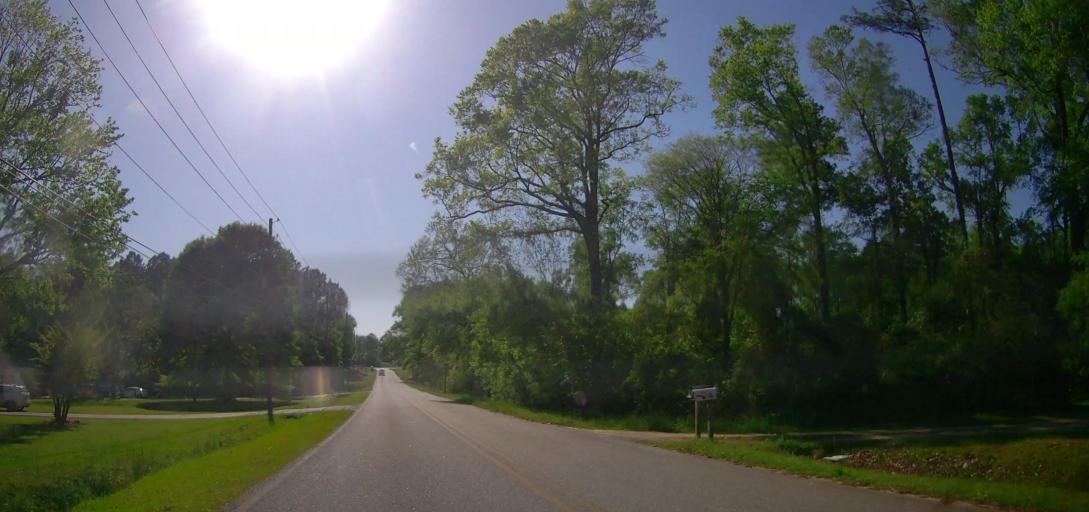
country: US
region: Georgia
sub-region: Houston County
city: Robins Air Force Base
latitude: 32.5438
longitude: -83.5922
